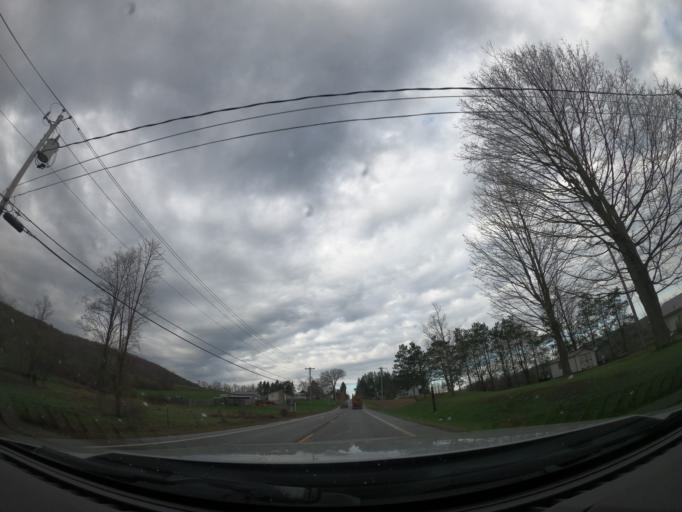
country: US
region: New York
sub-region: Madison County
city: Cazenovia
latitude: 42.7552
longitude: -75.8959
